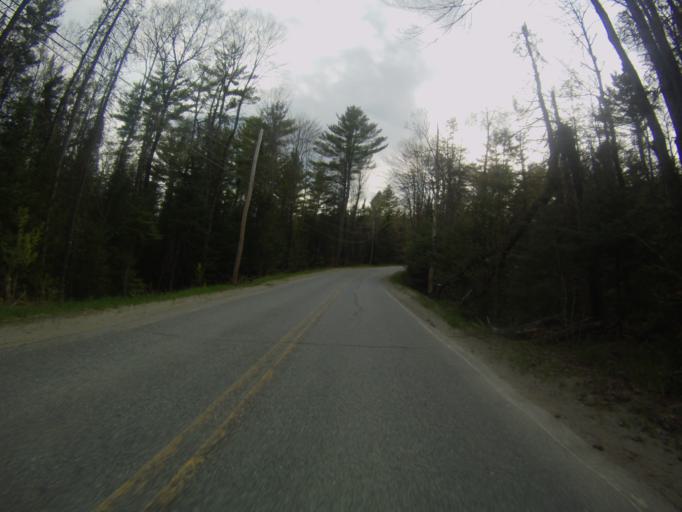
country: US
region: New York
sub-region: Warren County
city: Warrensburg
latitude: 43.8405
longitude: -73.8588
